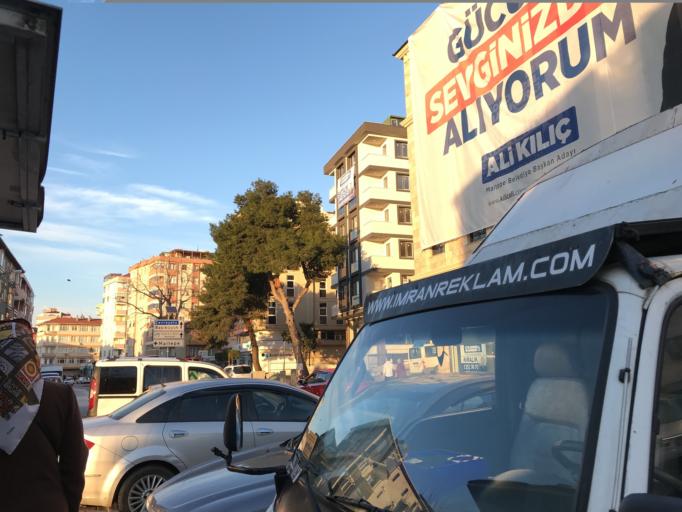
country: TR
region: Istanbul
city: Maltepe
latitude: 40.9274
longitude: 29.1336
